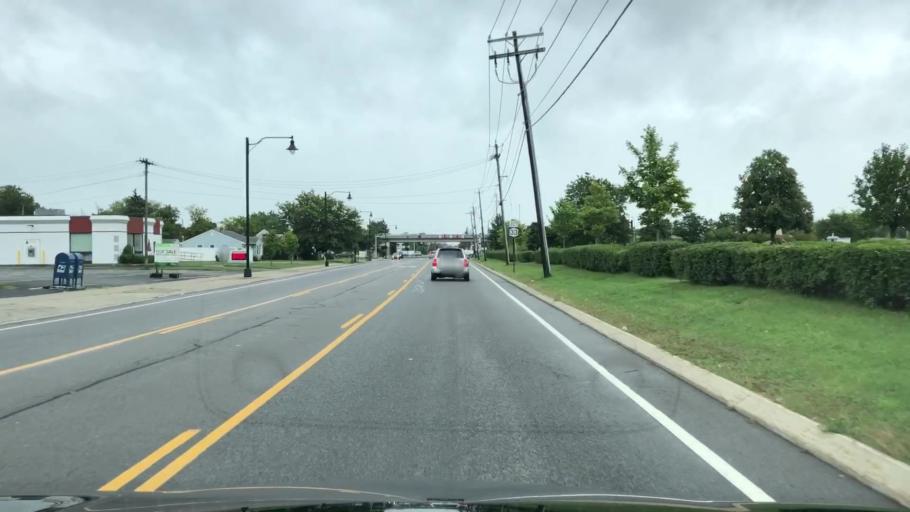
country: US
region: New York
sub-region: Erie County
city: Eggertsville
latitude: 42.9353
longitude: -78.7842
